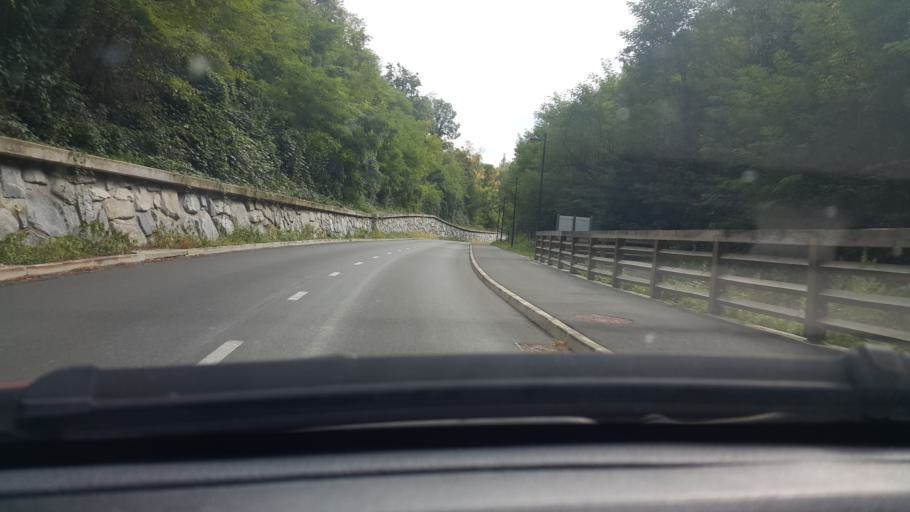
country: SI
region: Maribor
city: Maribor
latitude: 46.5688
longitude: 15.6444
